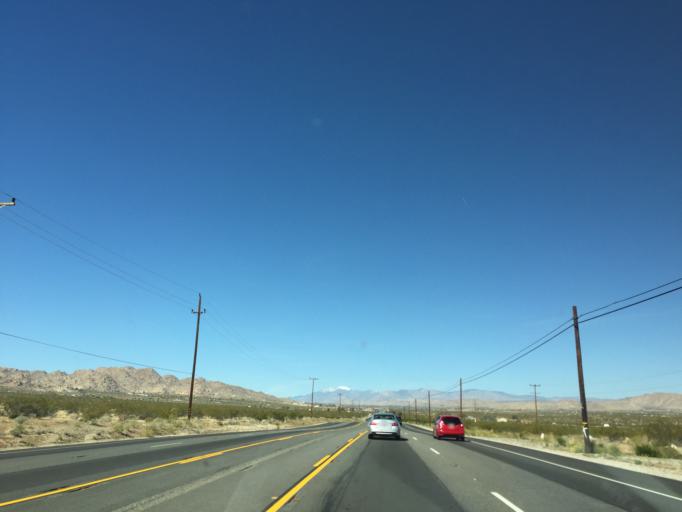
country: US
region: California
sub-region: San Bernardino County
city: Joshua Tree
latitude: 34.1352
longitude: -116.2372
